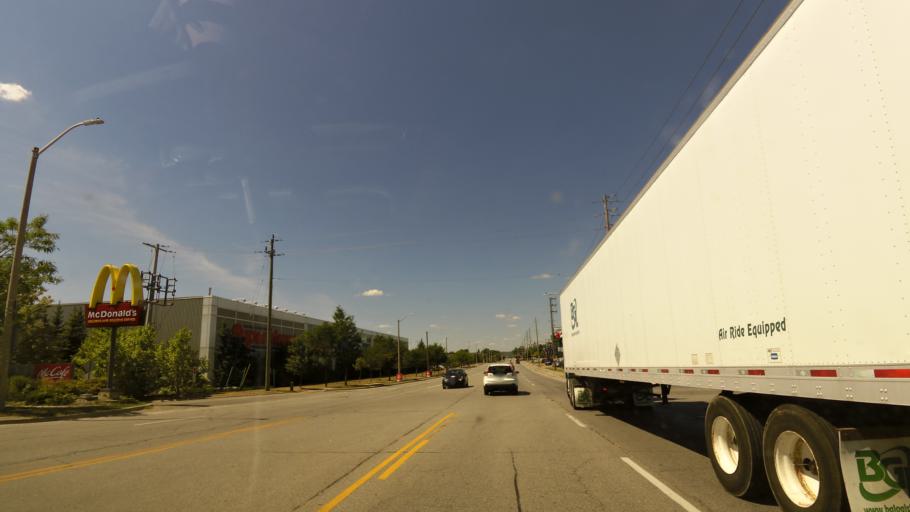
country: CA
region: Ontario
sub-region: Halton
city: Milton
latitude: 43.6513
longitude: -79.9048
